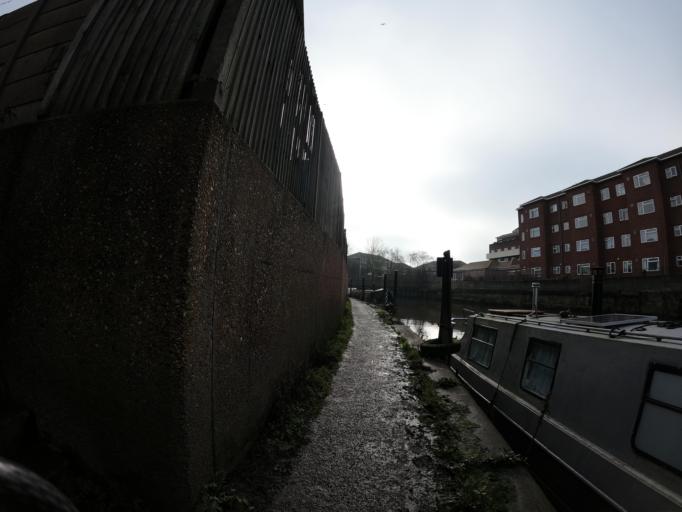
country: GB
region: England
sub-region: Greater London
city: Brentford
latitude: 51.4817
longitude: -0.3123
